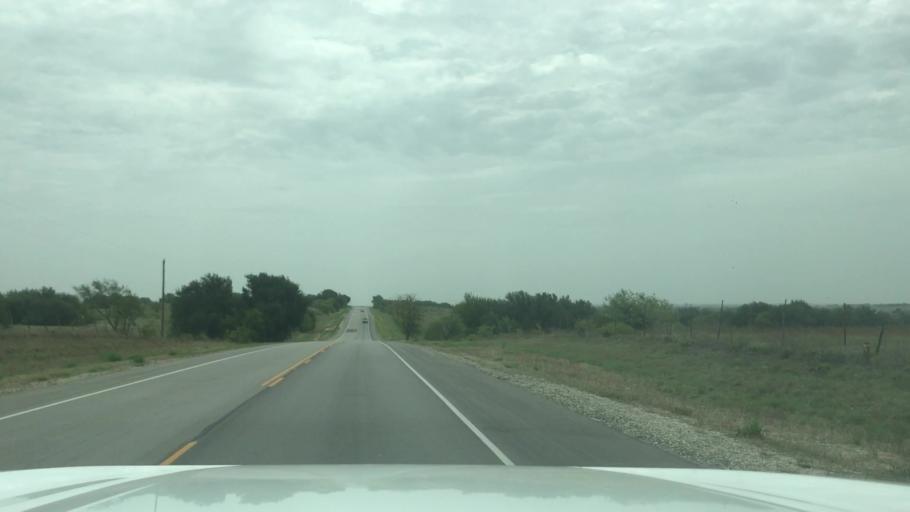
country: US
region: Texas
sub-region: Erath County
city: Dublin
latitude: 32.0828
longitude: -98.2484
